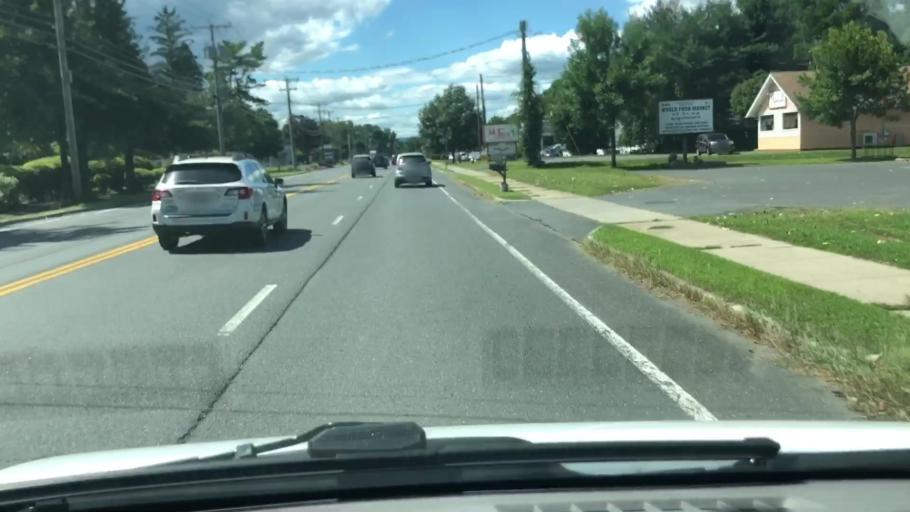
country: US
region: Massachusetts
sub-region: Hampshire County
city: Hadley
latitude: 42.3403
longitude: -72.6045
